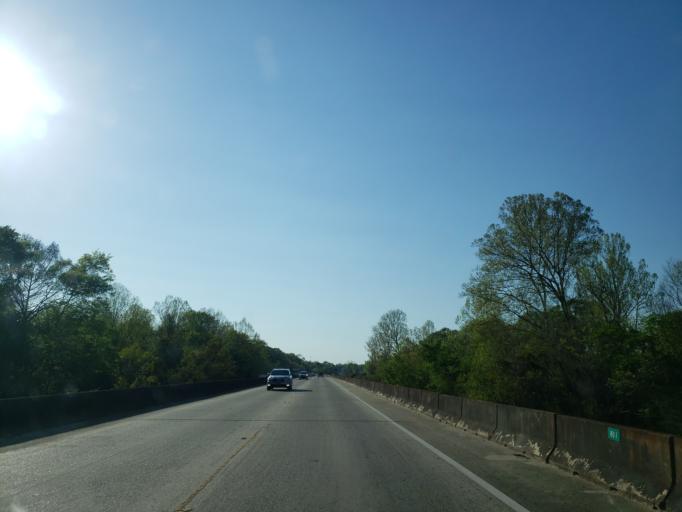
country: US
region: Mississippi
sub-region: Jones County
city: Laurel
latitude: 31.6805
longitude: -89.1148
